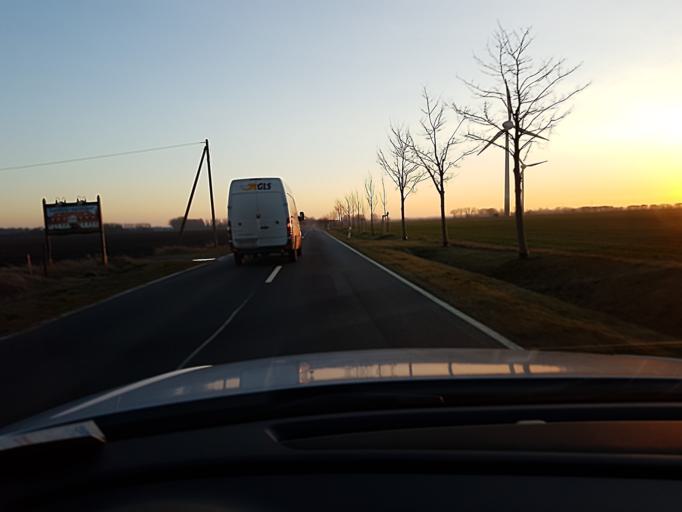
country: DE
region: Mecklenburg-Vorpommern
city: Wiek
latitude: 54.5978
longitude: 13.2903
